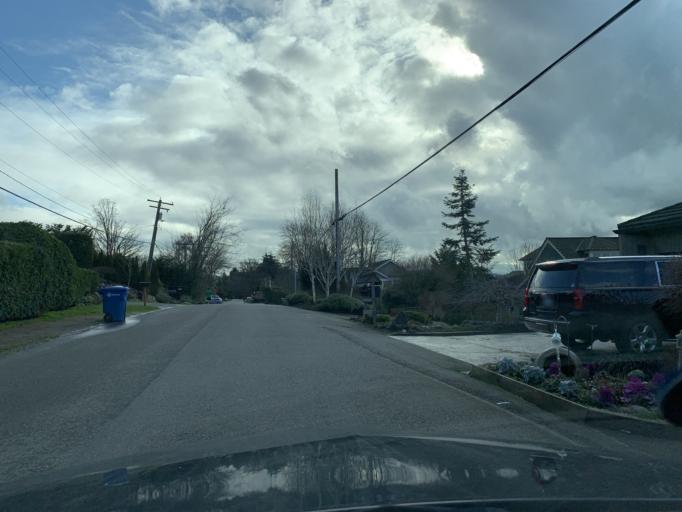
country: US
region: Washington
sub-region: King County
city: Mercer Island
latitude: 47.5862
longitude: -122.2527
